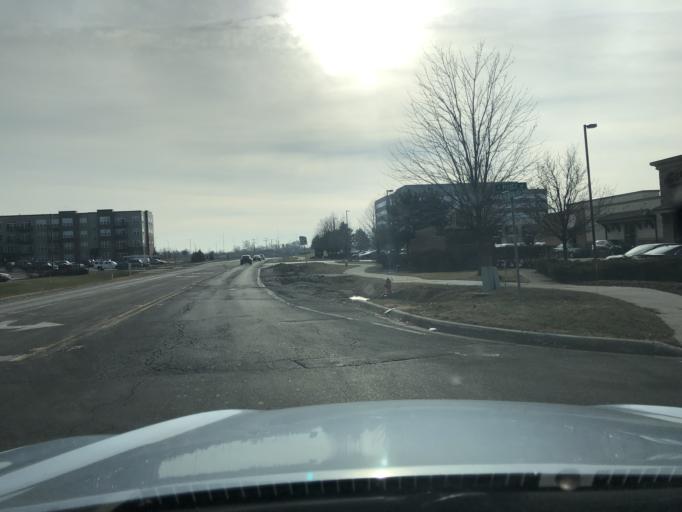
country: US
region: Illinois
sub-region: DuPage County
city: Itasca
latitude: 41.9877
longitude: -88.0015
